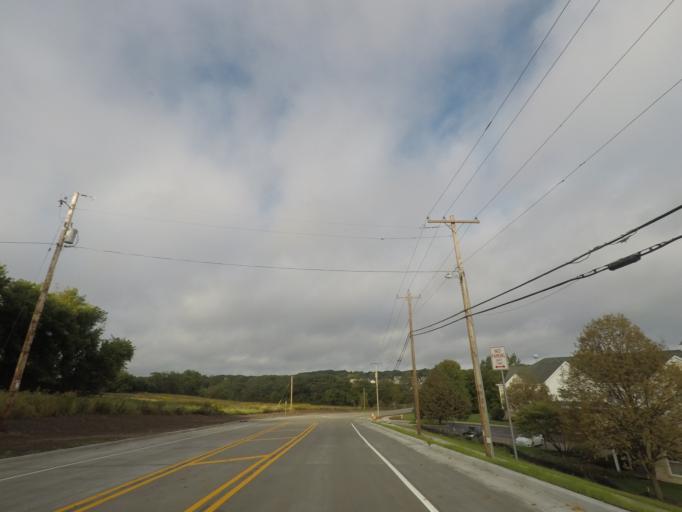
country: US
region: Wisconsin
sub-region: Waukesha County
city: Waukesha
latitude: 43.0321
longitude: -88.2747
